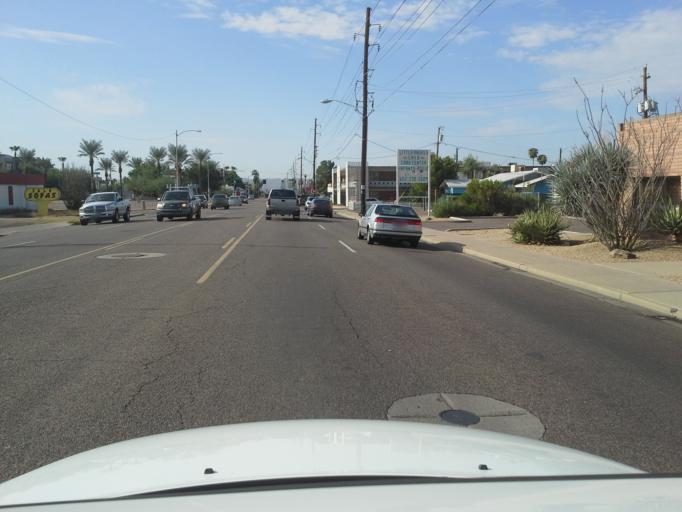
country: US
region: Arizona
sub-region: Maricopa County
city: Phoenix
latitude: 33.4896
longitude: -112.0477
